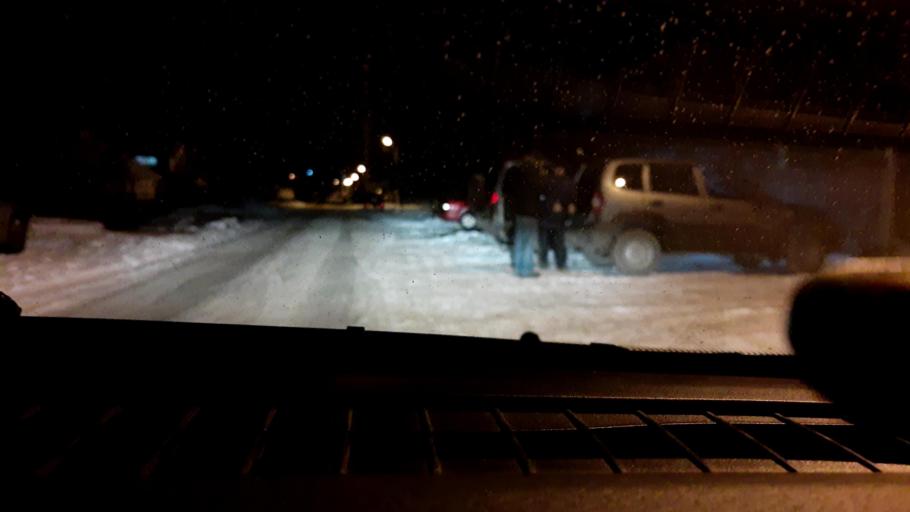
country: RU
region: Nizjnij Novgorod
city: Burevestnik
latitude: 56.1745
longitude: 43.7682
